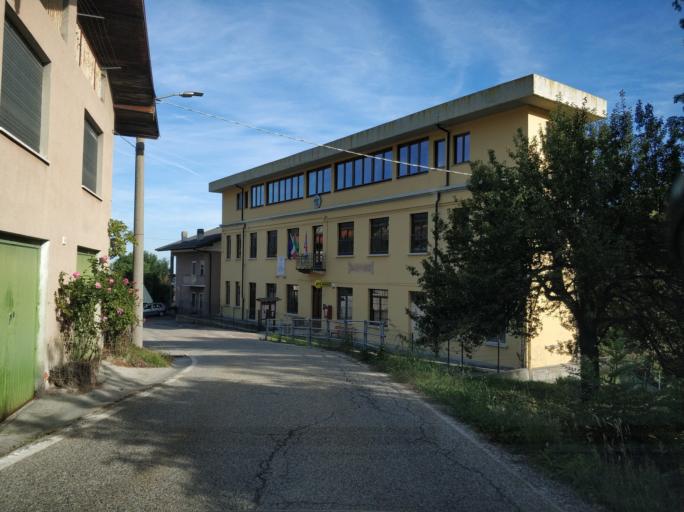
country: IT
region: Piedmont
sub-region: Provincia di Torino
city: Monastero di Lanzo
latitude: 45.3018
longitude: 7.4388
